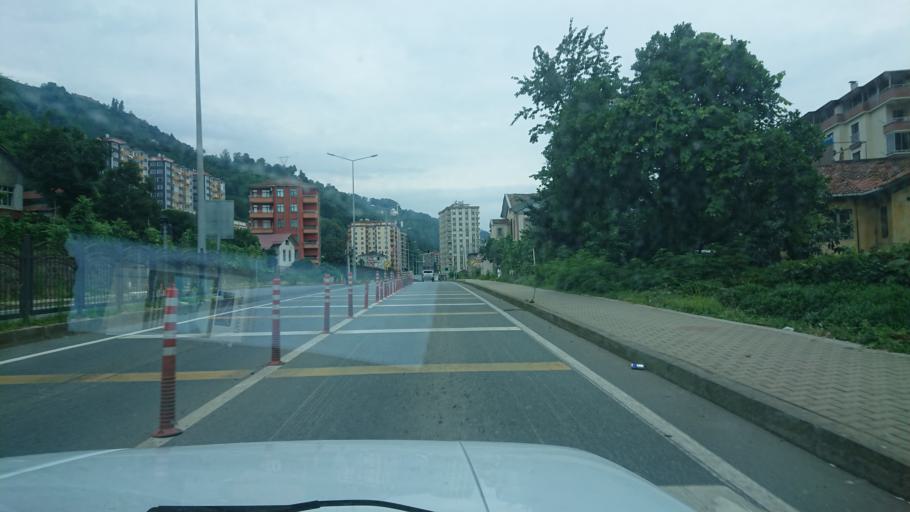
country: TR
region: Rize
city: Gundogdu
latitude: 41.0360
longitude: 40.5653
